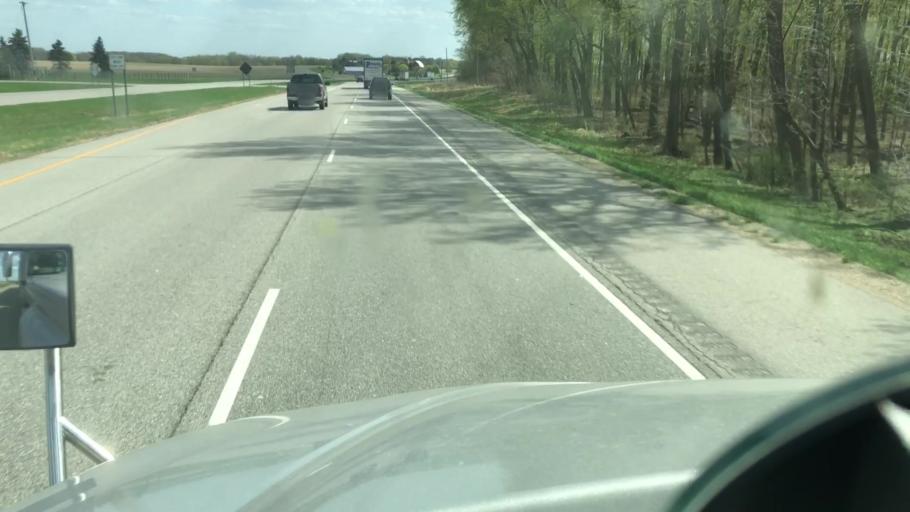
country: US
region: Minnesota
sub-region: Le Sueur County
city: Le Sueur
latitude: 44.5379
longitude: -93.8485
